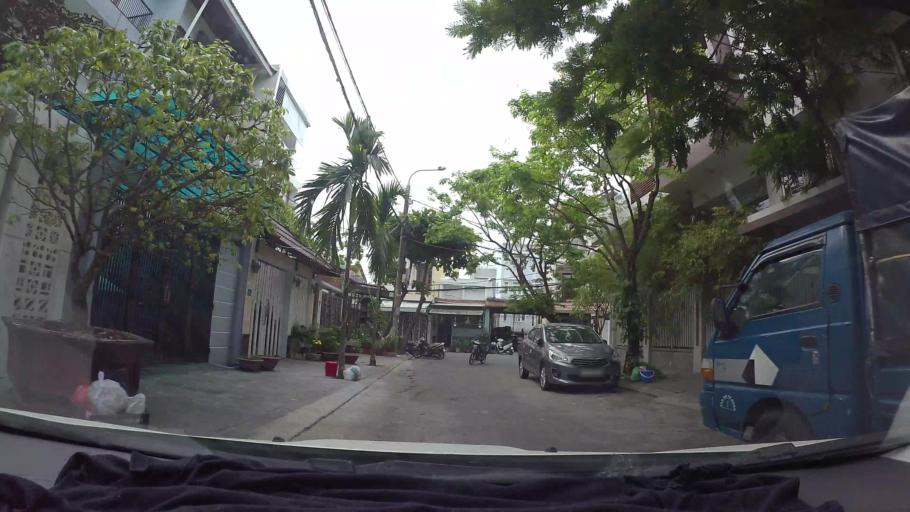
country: VN
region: Da Nang
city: Thanh Khe
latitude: 16.0699
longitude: 108.1922
